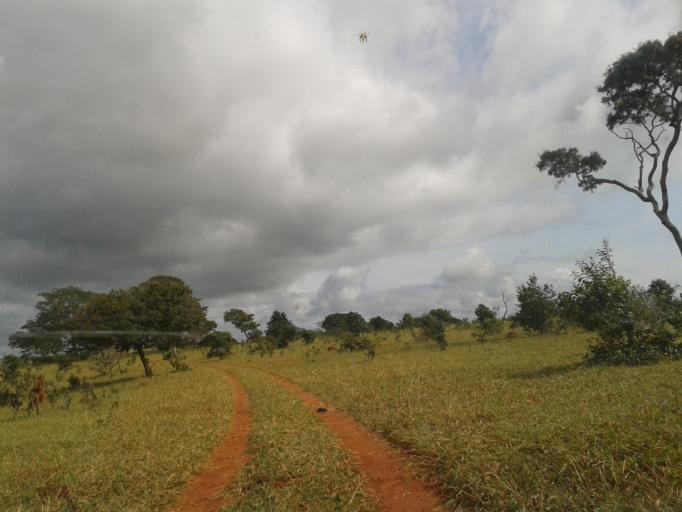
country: BR
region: Minas Gerais
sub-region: Campina Verde
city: Campina Verde
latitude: -19.4156
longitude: -49.6675
